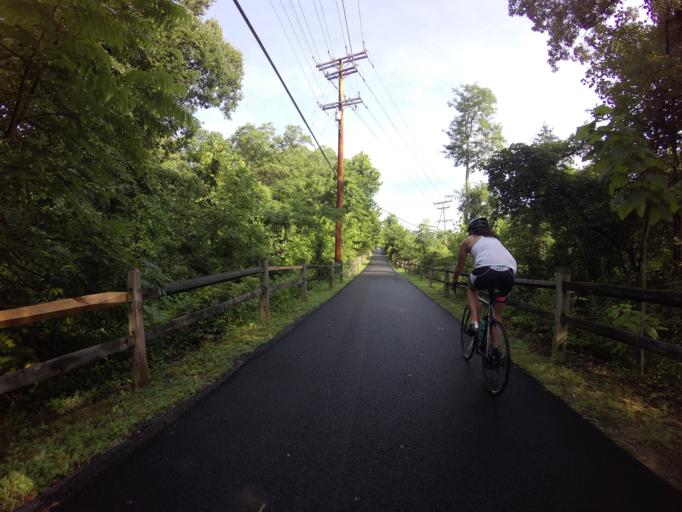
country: US
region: Maryland
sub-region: Anne Arundel County
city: Pasadena
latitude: 39.1073
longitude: -76.5762
